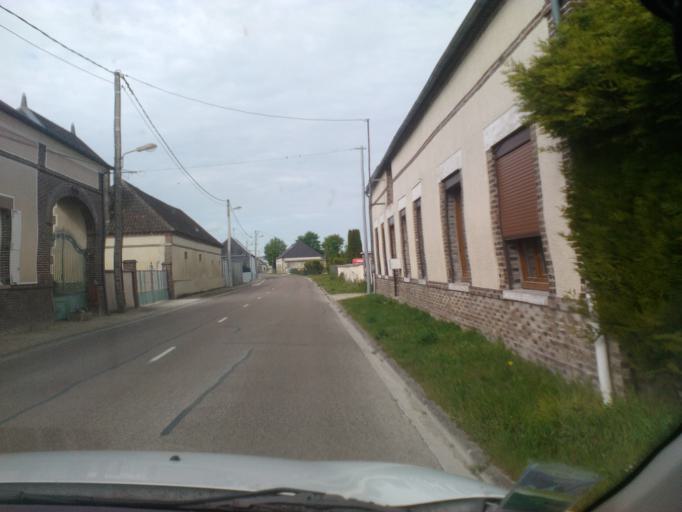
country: FR
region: Champagne-Ardenne
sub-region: Departement de l'Aube
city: Marigny-le-Chatel
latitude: 48.3776
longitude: 3.7811
